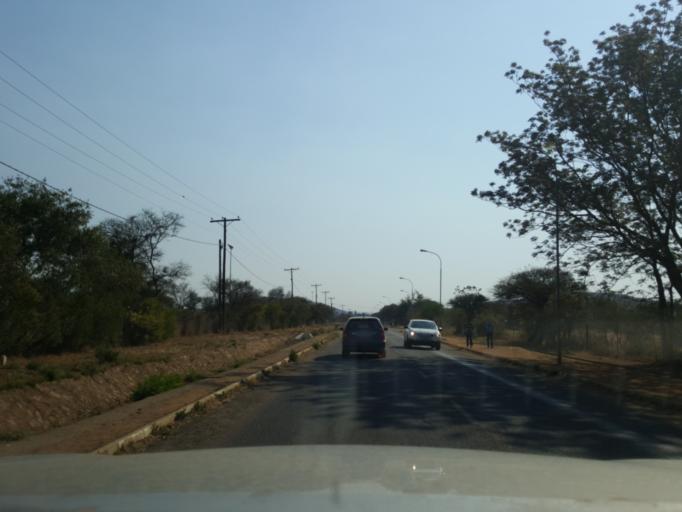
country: BW
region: South East
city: Lobatse
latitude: -25.1976
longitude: 25.6919
